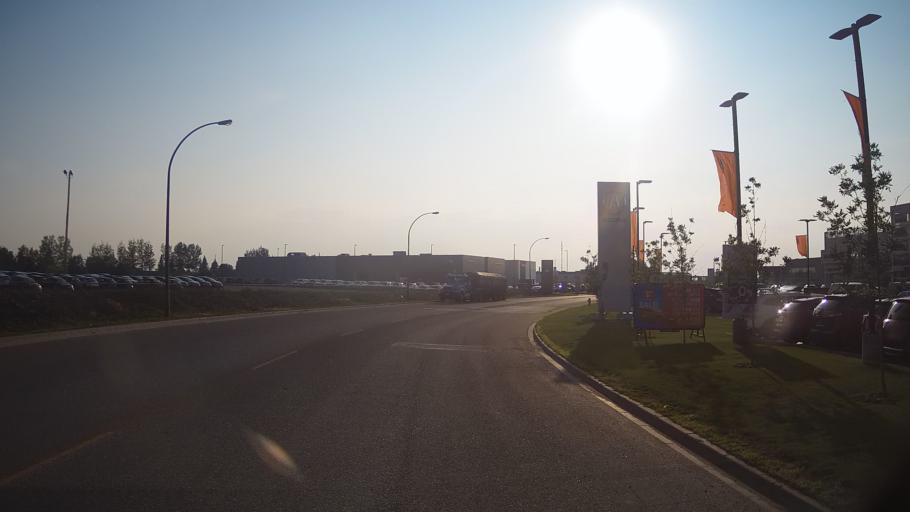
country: CA
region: Saskatchewan
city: Saskatoon
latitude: 52.0835
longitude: -106.6484
